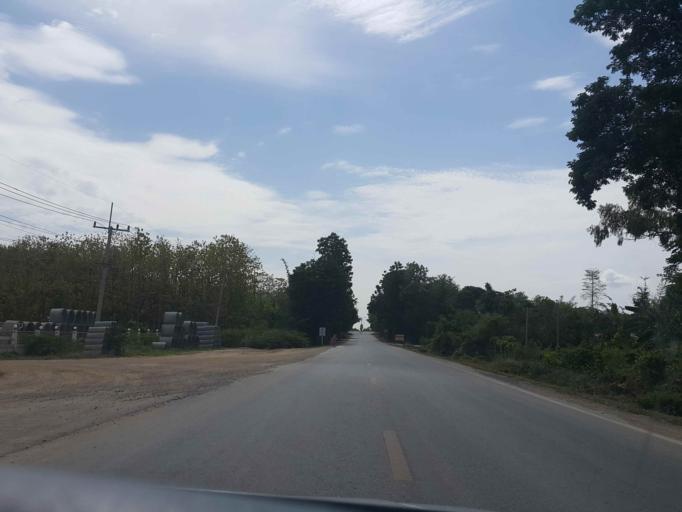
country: TH
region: Sukhothai
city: Thung Saliam
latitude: 17.3317
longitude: 99.5312
